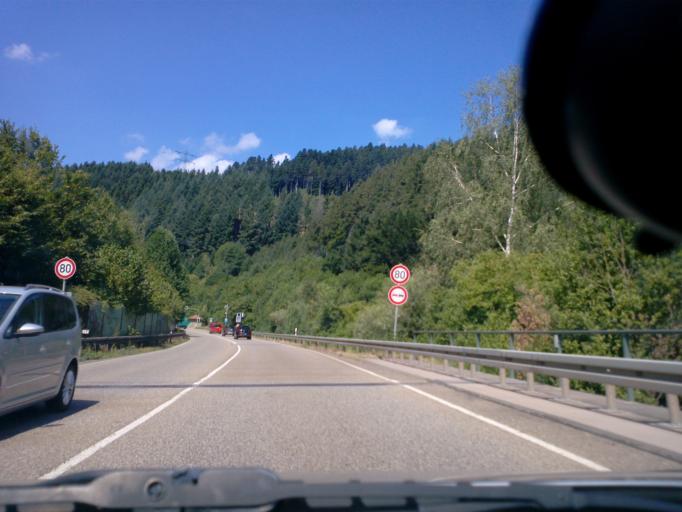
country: DE
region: Baden-Wuerttemberg
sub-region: Freiburg Region
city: Hausach
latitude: 48.2889
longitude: 8.1862
